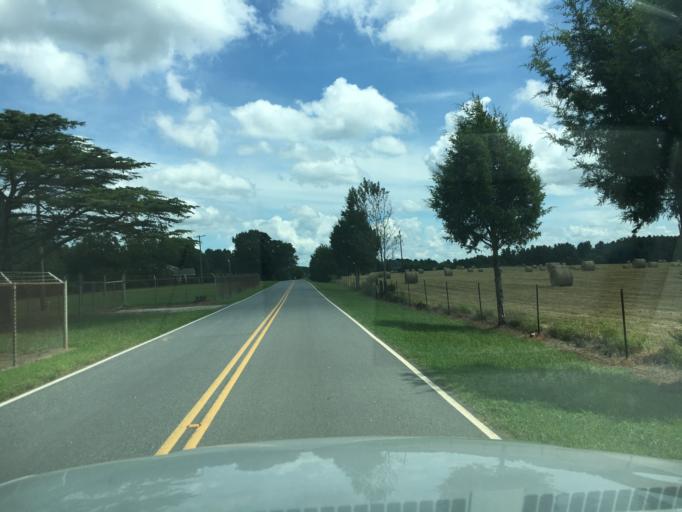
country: US
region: South Carolina
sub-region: Anderson County
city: Belton
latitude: 34.5463
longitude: -82.4563
